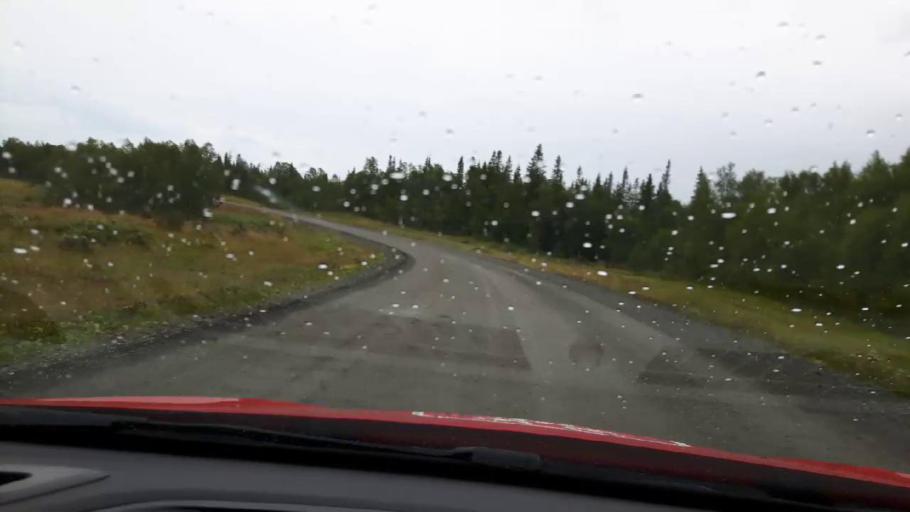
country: NO
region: Nord-Trondelag
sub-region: Meraker
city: Meraker
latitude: 63.5607
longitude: 12.2945
